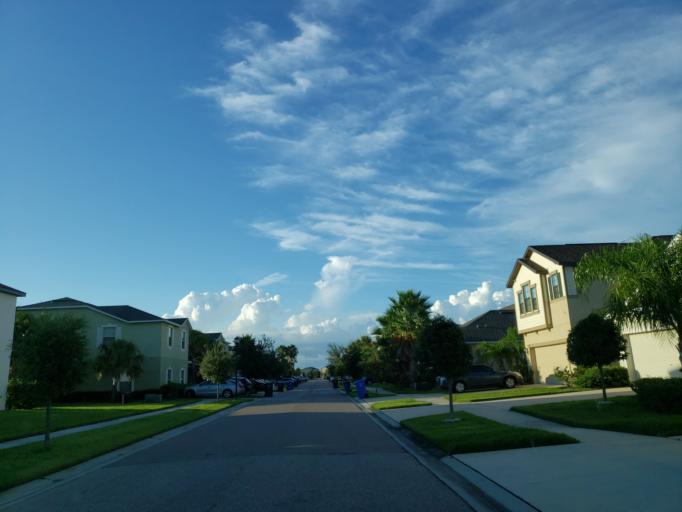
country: US
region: Florida
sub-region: Hillsborough County
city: Ruskin
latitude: 27.7311
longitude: -82.4084
